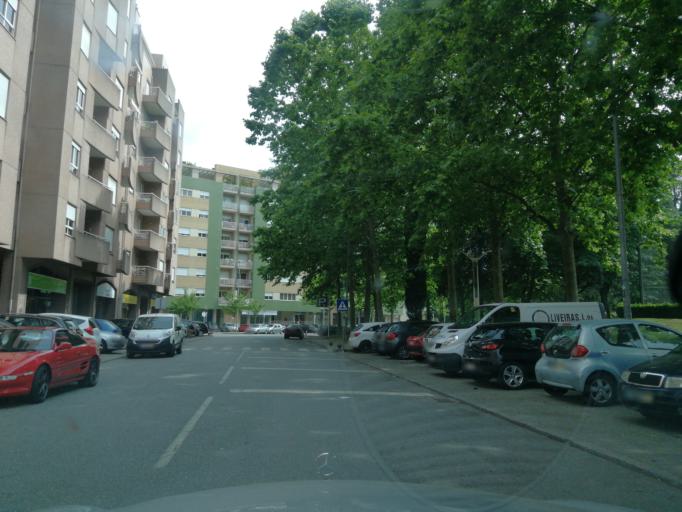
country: PT
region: Braga
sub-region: Vila Nova de Famalicao
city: Vila Nova de Famalicao
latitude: 41.4050
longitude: -8.5205
